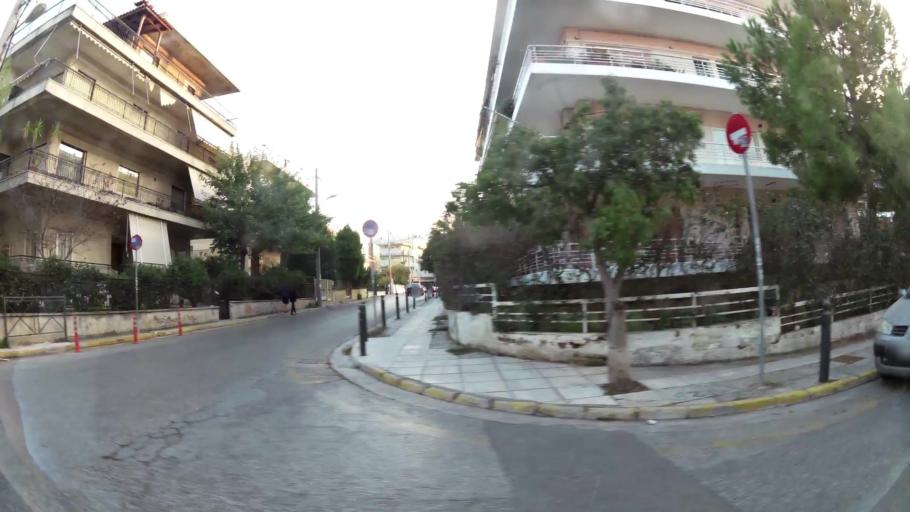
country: GR
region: Attica
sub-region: Nomarchia Athinas
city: Agia Paraskevi
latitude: 38.0142
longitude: 23.8335
